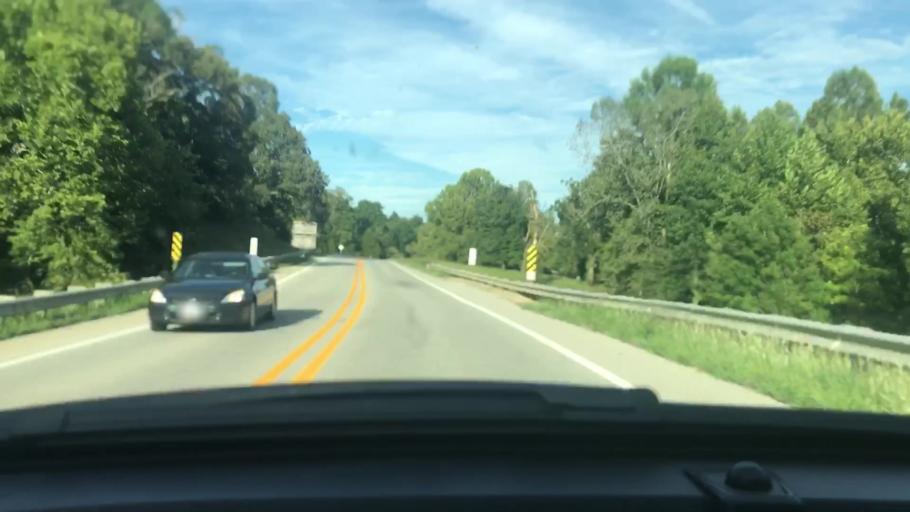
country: US
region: Arkansas
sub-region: Sharp County
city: Cherokee Village
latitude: 36.2735
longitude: -91.3533
